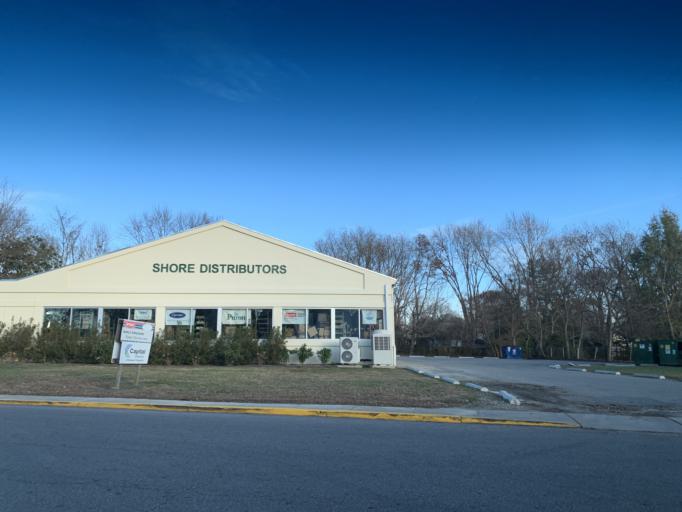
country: US
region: Maryland
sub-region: Kent County
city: Chestertown
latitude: 39.2146
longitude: -76.0701
